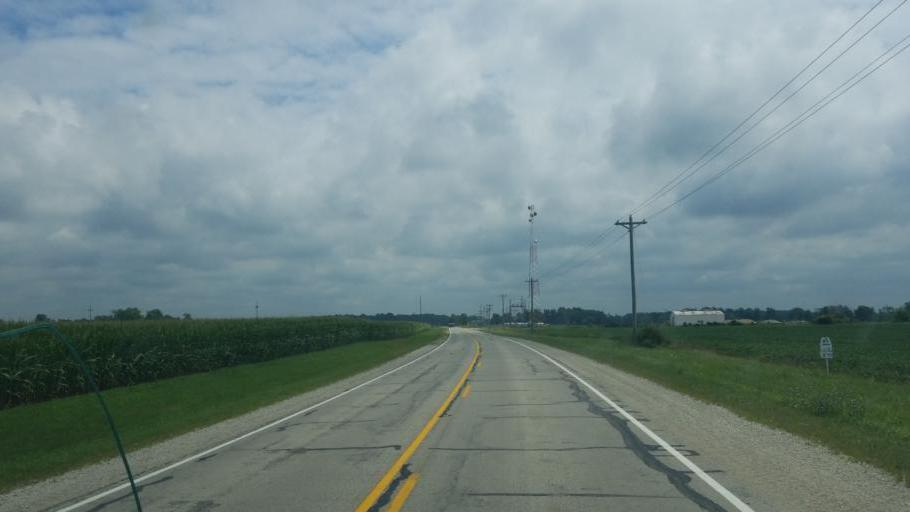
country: US
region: Indiana
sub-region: Huntington County
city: Warren
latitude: 40.6683
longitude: -85.4438
